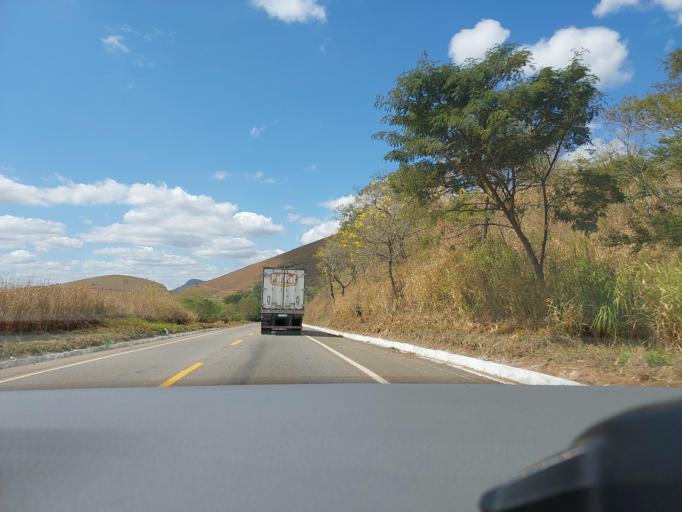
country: BR
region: Minas Gerais
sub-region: Muriae
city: Muriae
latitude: -21.1270
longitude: -42.2413
